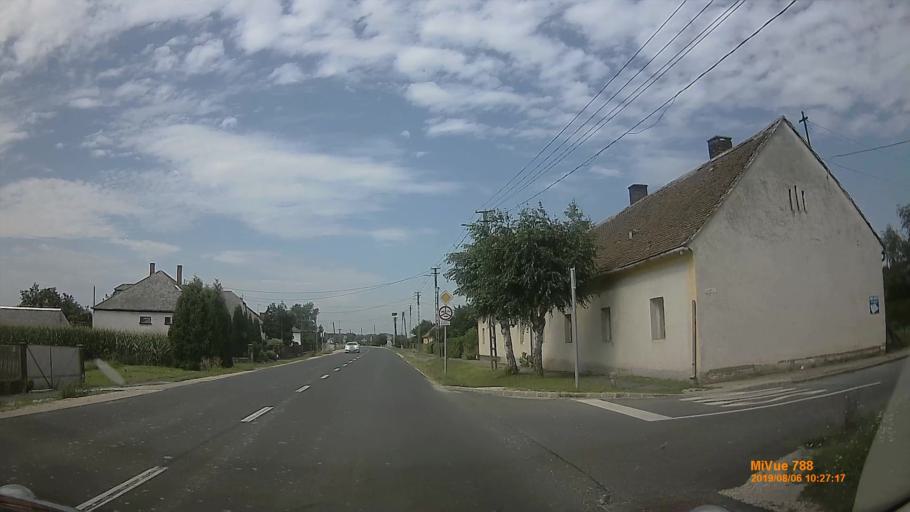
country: HU
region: Vas
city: Kormend
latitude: 47.0438
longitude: 16.6706
